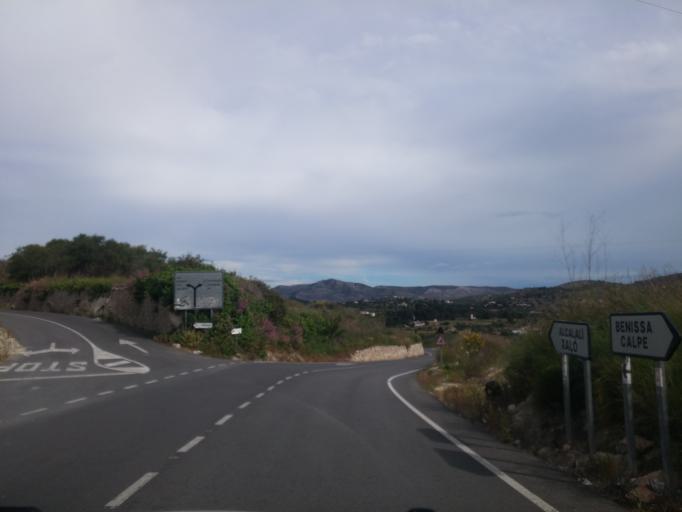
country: ES
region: Valencia
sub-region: Provincia de Alicante
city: Benissa
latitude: 38.7101
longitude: 0.0375
